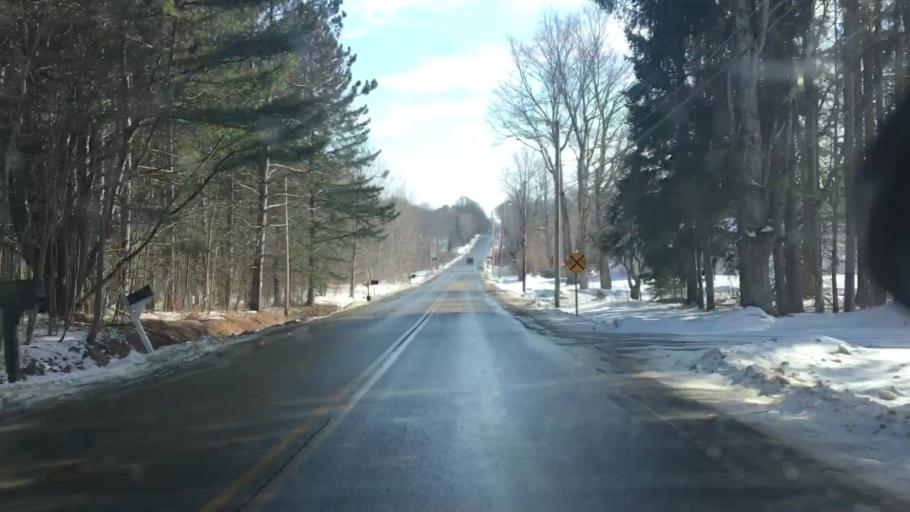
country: US
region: Maine
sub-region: Penobscot County
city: Hermon
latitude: 44.8519
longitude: -68.8440
